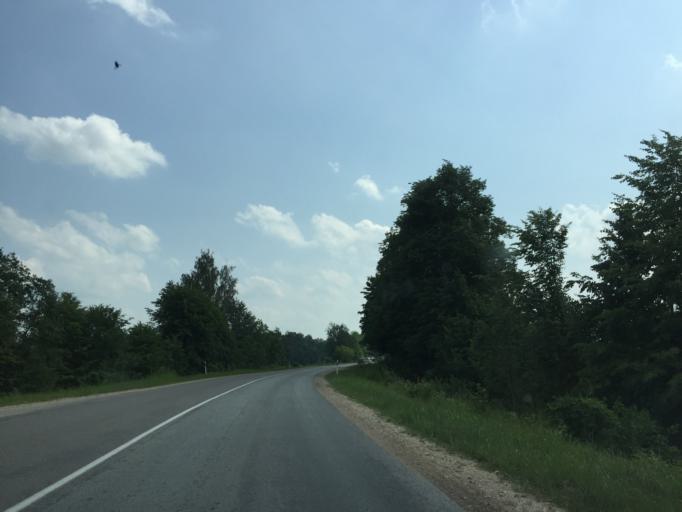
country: LV
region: Jelgava
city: Jelgava
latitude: 56.6928
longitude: 23.7185
